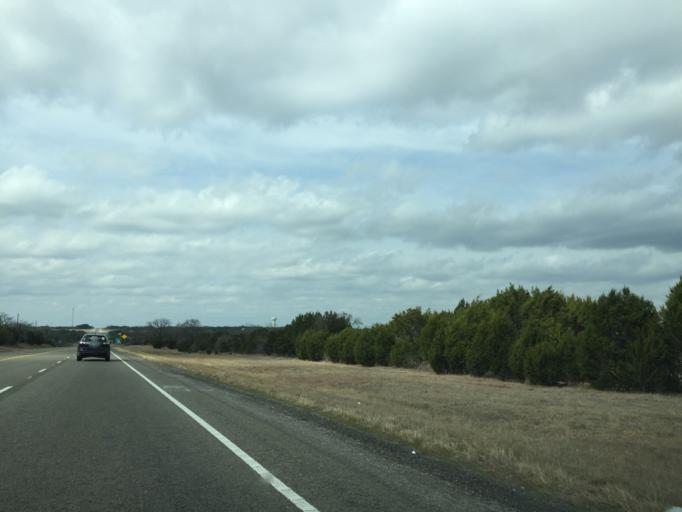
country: US
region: Texas
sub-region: Burnet County
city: Meadowlakes
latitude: 30.5048
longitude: -98.2785
